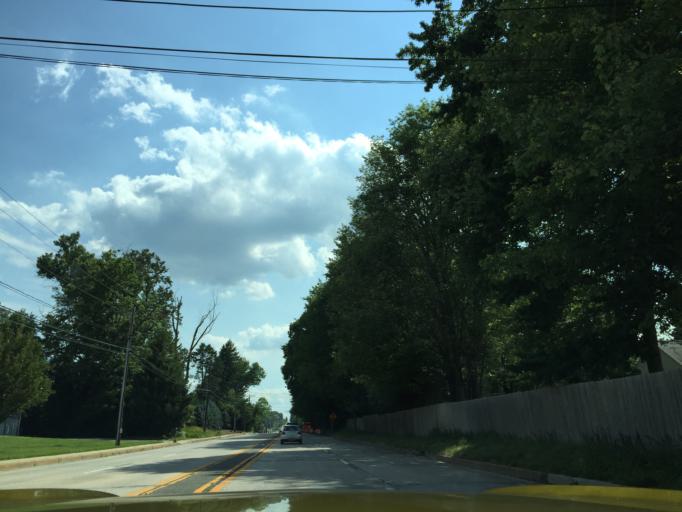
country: US
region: Delaware
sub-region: New Castle County
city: Claymont
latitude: 39.8194
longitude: -75.5052
